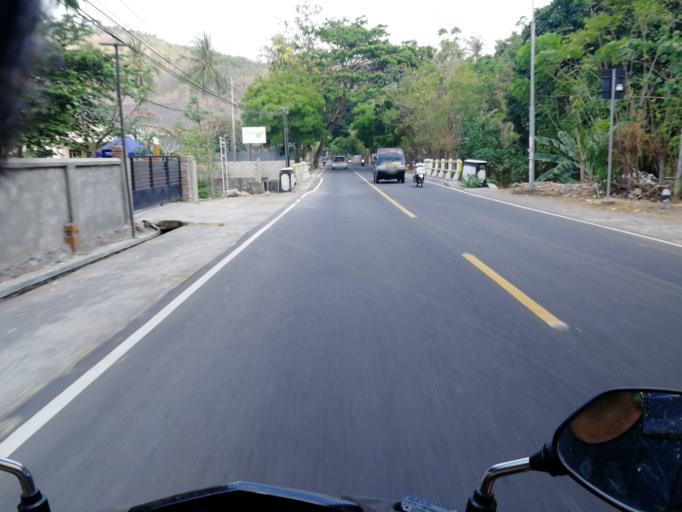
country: ID
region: West Nusa Tenggara
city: Karangsubagan
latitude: -8.4876
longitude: 116.0395
